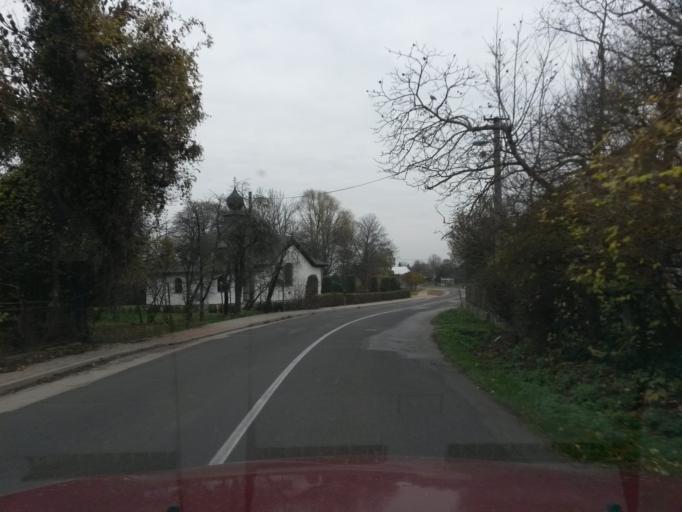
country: SK
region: Kosicky
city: Trebisov
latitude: 48.6342
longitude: 21.6624
